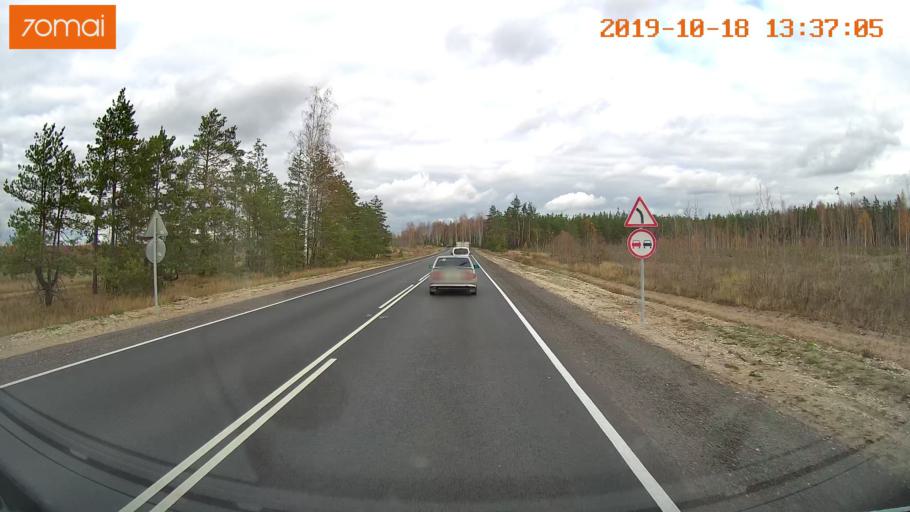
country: RU
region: Rjazan
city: Solotcha
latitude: 54.8763
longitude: 39.9913
